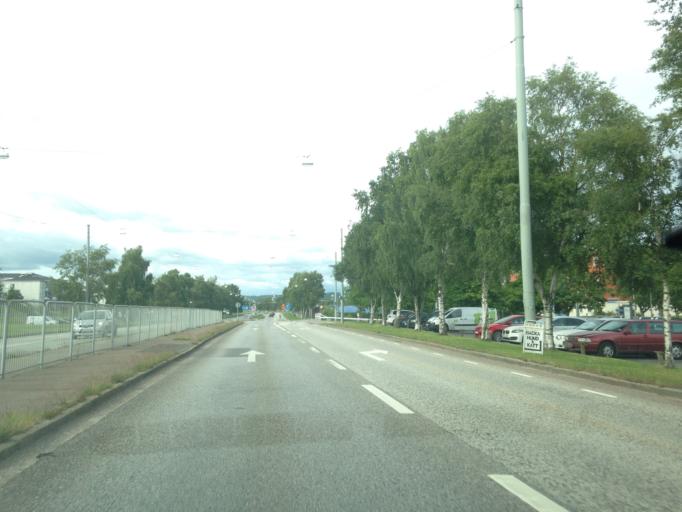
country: SE
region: Vaestra Goetaland
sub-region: Goteborg
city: Goeteborg
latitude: 57.7448
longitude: 11.9764
